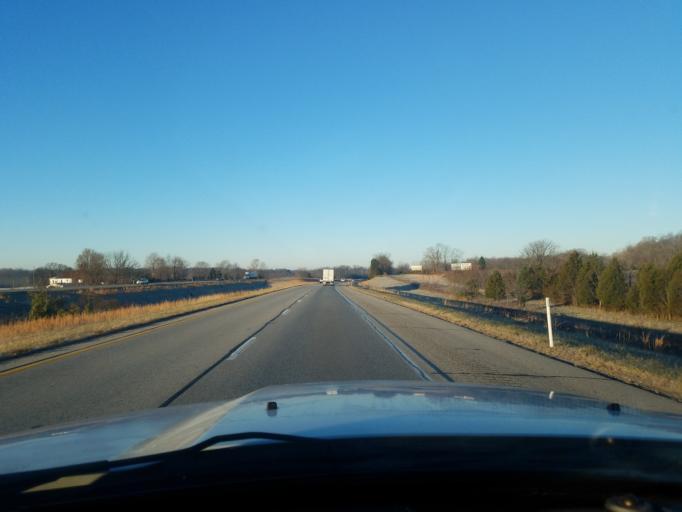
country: US
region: Indiana
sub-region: Harrison County
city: Corydon
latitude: 38.2480
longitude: -86.0663
